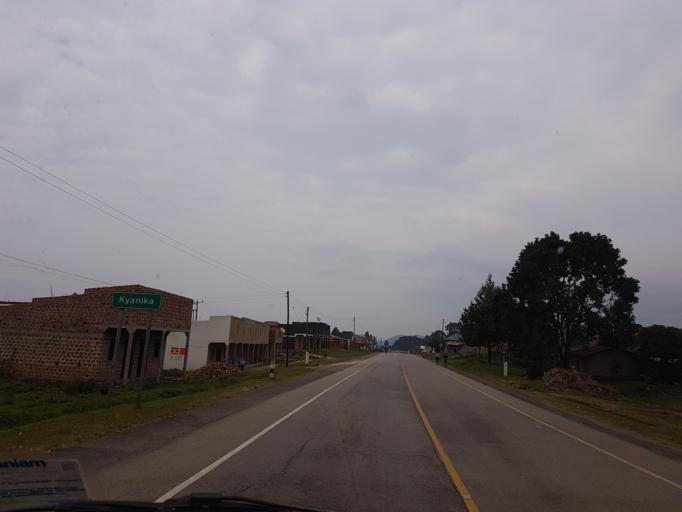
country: UG
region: Western Region
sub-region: Kisoro District
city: Kisoro
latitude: -1.3337
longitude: 29.7365
